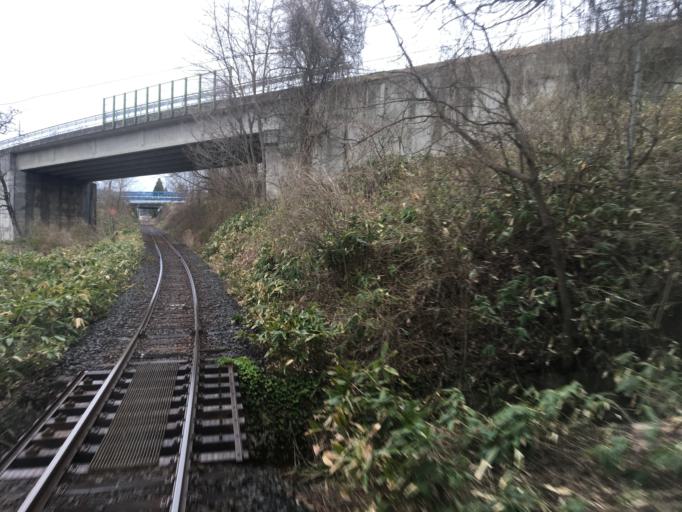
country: JP
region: Akita
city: Takanosu
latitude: 40.1297
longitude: 140.3788
